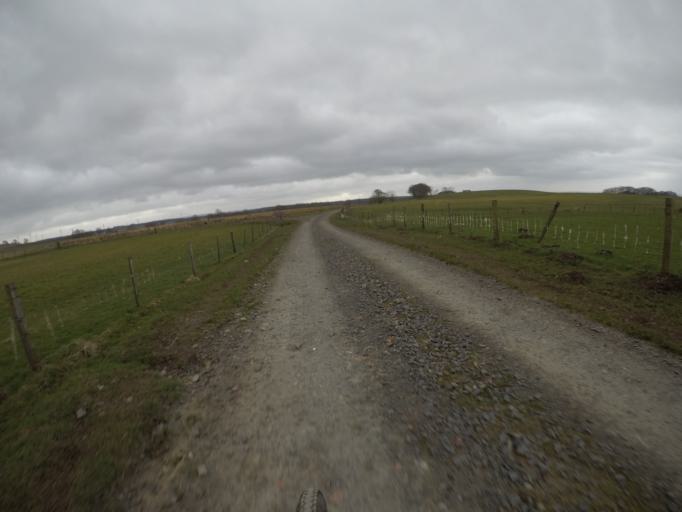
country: GB
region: Scotland
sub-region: East Ayrshire
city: Galston
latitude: 55.6709
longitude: -4.3731
